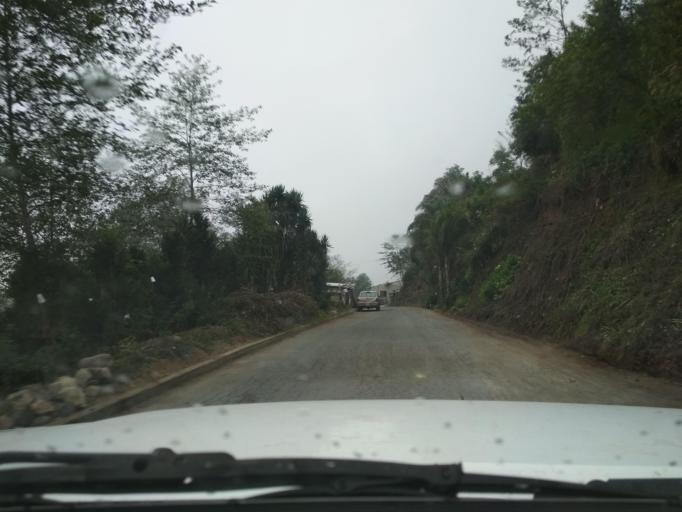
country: MX
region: Veracruz
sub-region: La Perla
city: Metlac Hernandez (Metlac Primero)
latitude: 18.9499
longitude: -97.1644
